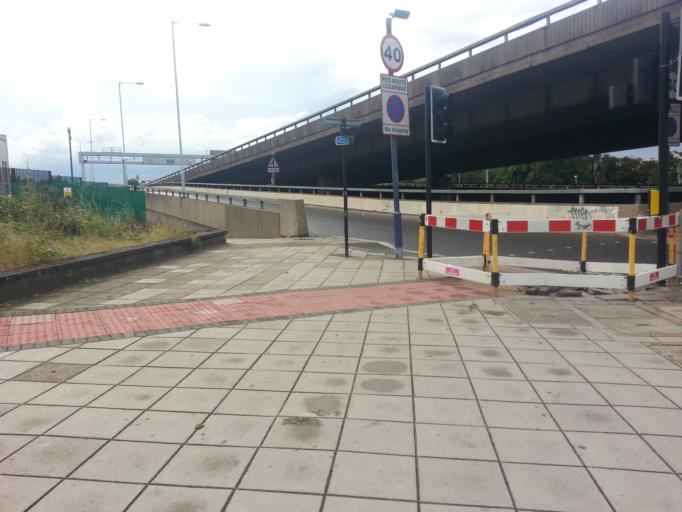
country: GB
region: England
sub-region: Greater London
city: Hammersmith
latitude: 51.5148
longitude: -0.2263
